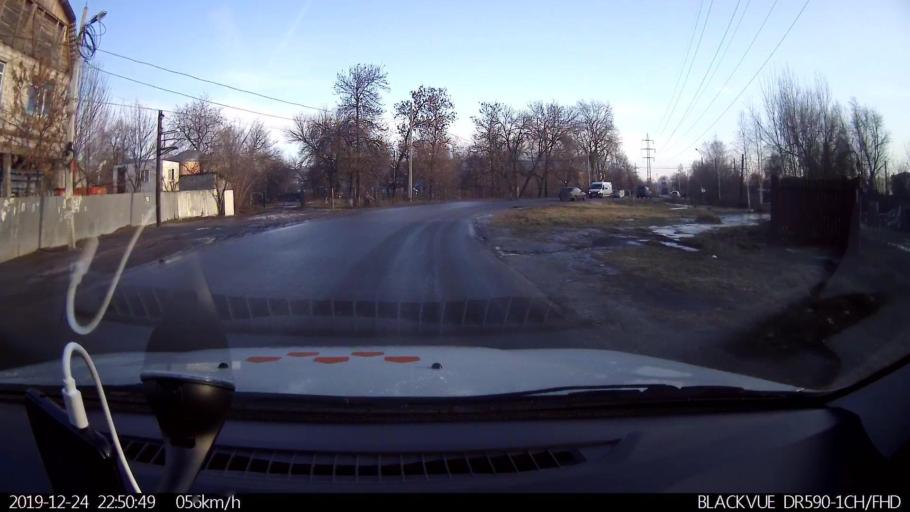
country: RU
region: Nizjnij Novgorod
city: Nizhniy Novgorod
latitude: 56.2900
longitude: 43.9030
